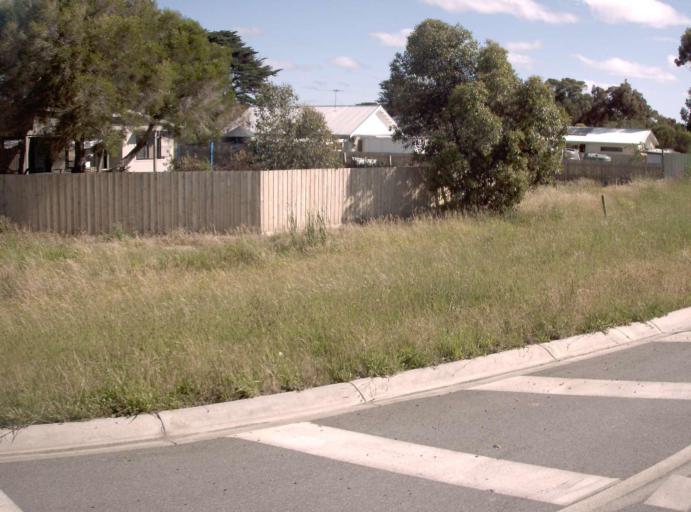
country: AU
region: Victoria
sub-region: Bass Coast
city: North Wonthaggi
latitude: -38.4788
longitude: 145.4702
